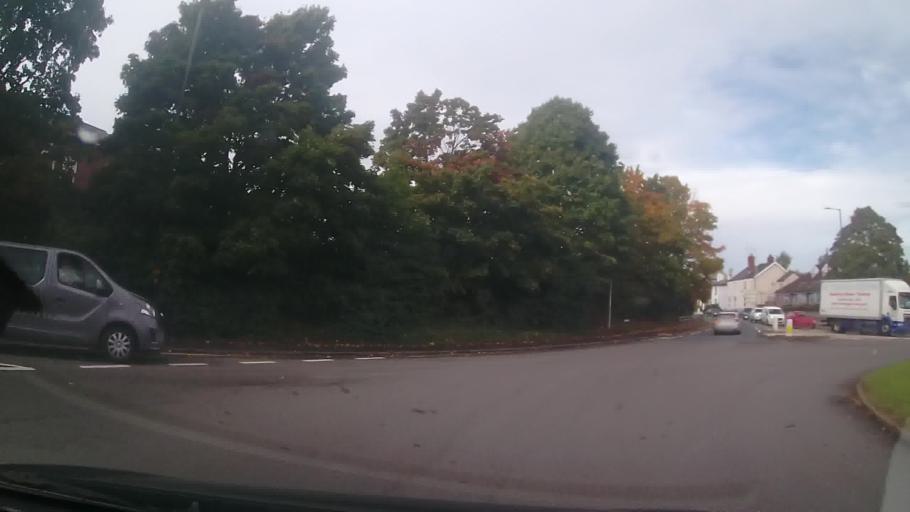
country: GB
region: England
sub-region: Worcestershire
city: Kidderminster
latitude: 52.3911
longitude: -2.2606
